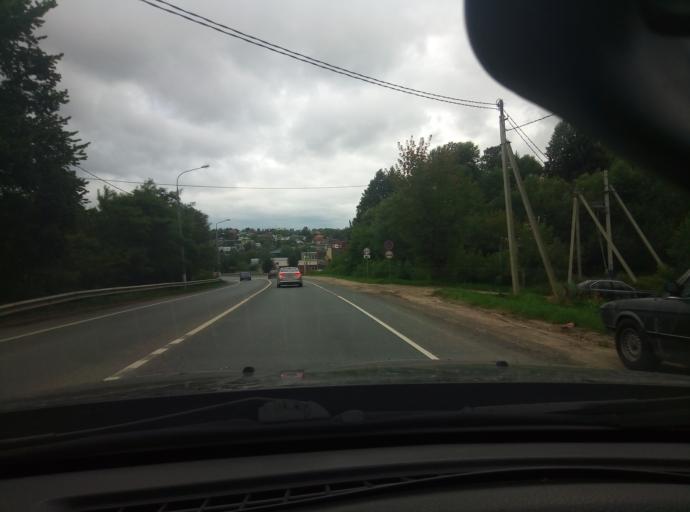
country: RU
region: Moskovskaya
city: Danki
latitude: 54.9113
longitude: 37.4958
